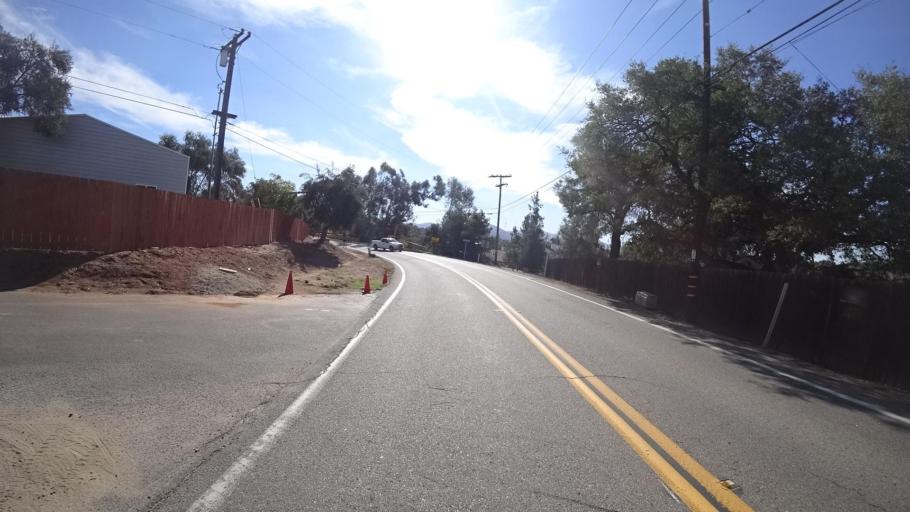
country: US
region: California
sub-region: San Diego County
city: Alpine
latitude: 32.8159
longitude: -116.7806
